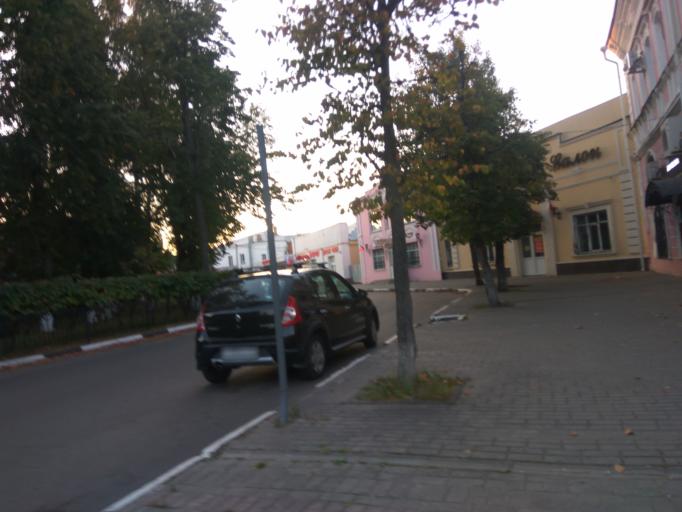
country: RU
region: Moskovskaya
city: Yegor'yevsk
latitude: 55.3836
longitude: 39.0367
